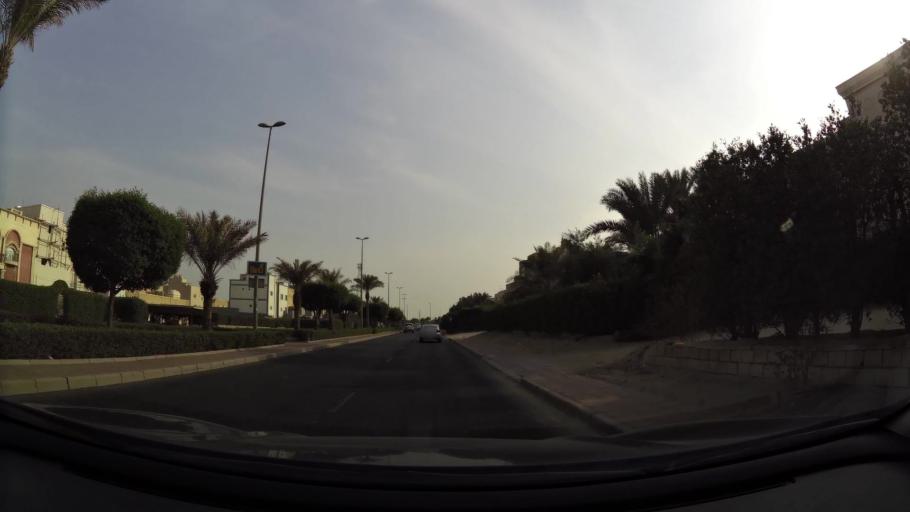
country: KW
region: Mubarak al Kabir
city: Sabah as Salim
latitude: 29.2396
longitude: 48.0613
